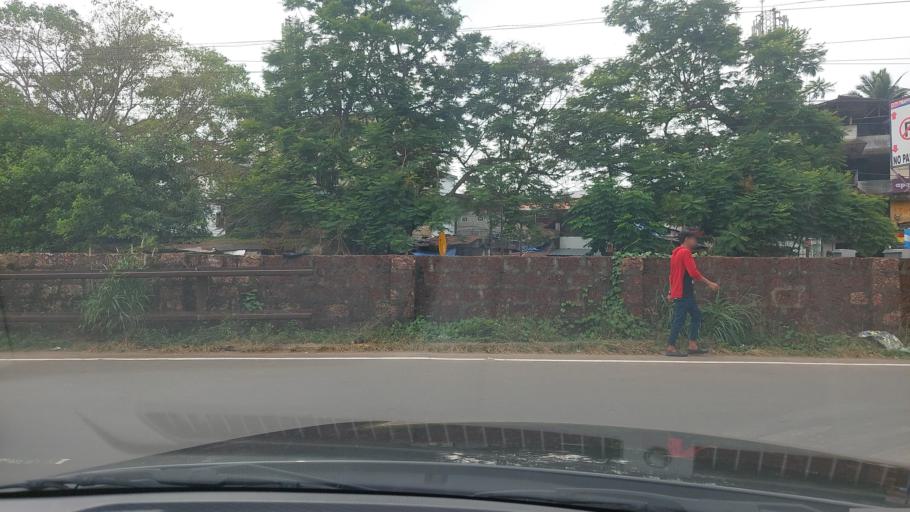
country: IN
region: Kerala
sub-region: Kozhikode
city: Kozhikode
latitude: 11.2526
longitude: 75.7793
